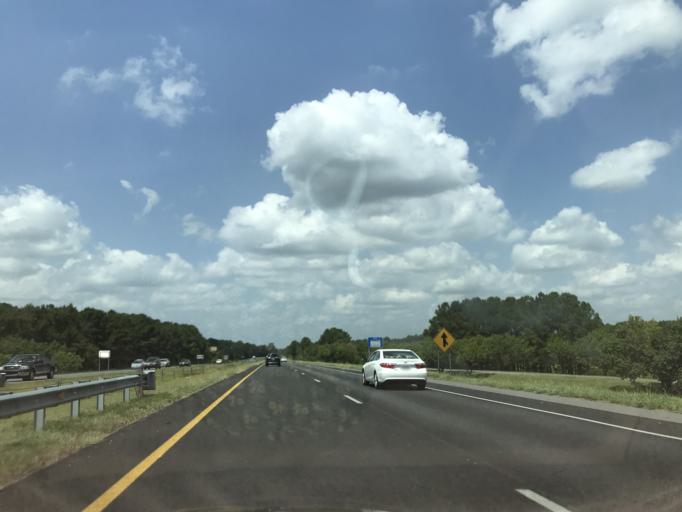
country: US
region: North Carolina
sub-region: Duplin County
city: Wallace
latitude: 34.7700
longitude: -77.9654
